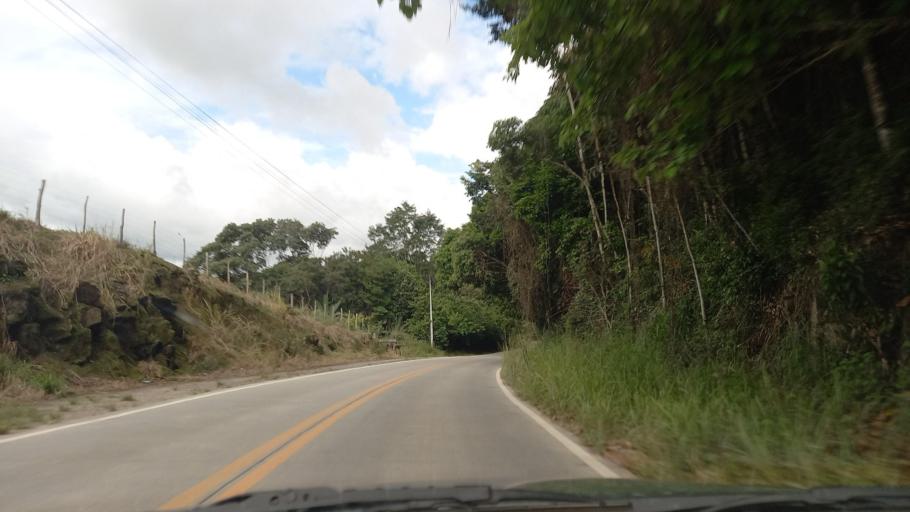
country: BR
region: Pernambuco
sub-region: Maraial
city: Maraial
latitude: -8.7803
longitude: -35.9144
